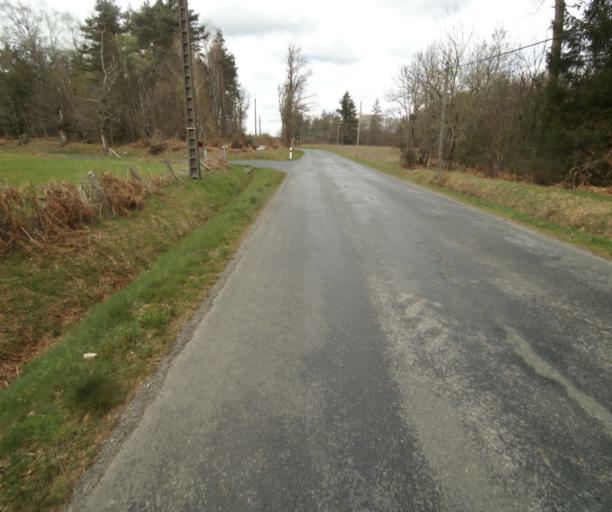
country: FR
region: Limousin
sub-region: Departement de la Correze
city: Argentat
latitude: 45.2162
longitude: 1.9261
